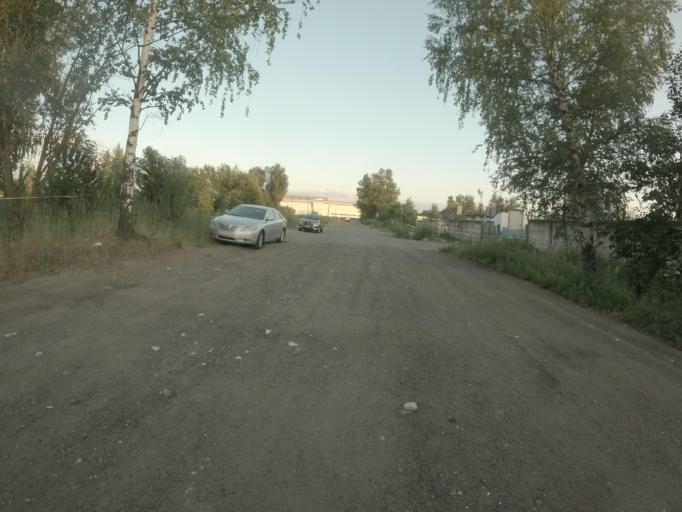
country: RU
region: St.-Petersburg
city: Krasnogvargeisky
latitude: 59.9505
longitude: 30.4571
